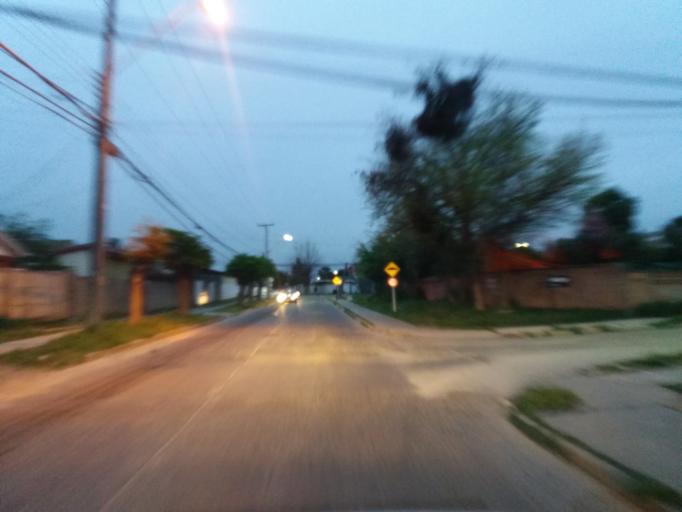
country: CL
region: Valparaiso
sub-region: Provincia de Marga Marga
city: Limache
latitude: -33.0061
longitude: -71.2633
